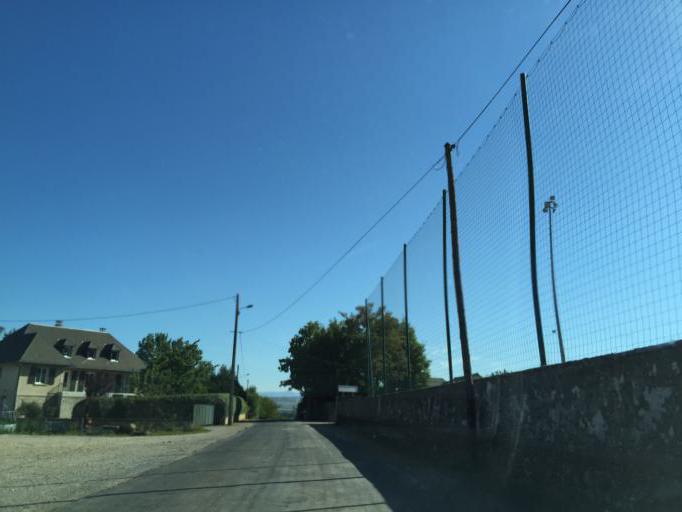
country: FR
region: Midi-Pyrenees
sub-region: Departement de l'Aveyron
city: Laissac
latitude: 44.3796
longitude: 2.8152
